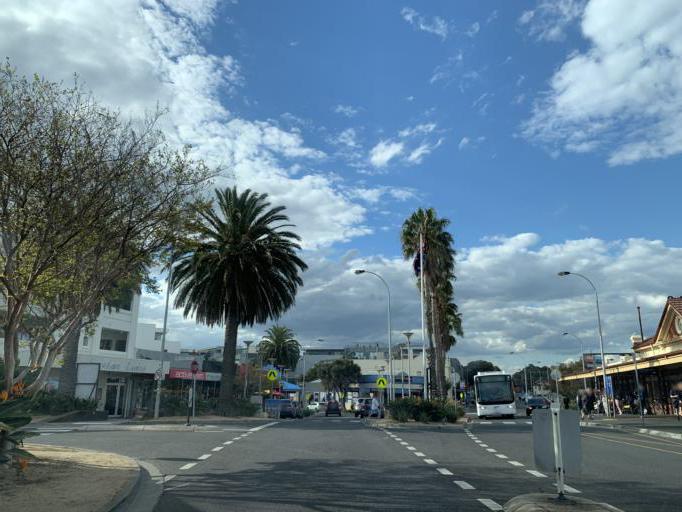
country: AU
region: Victoria
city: Hampton
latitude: -37.9506
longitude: 145.0042
